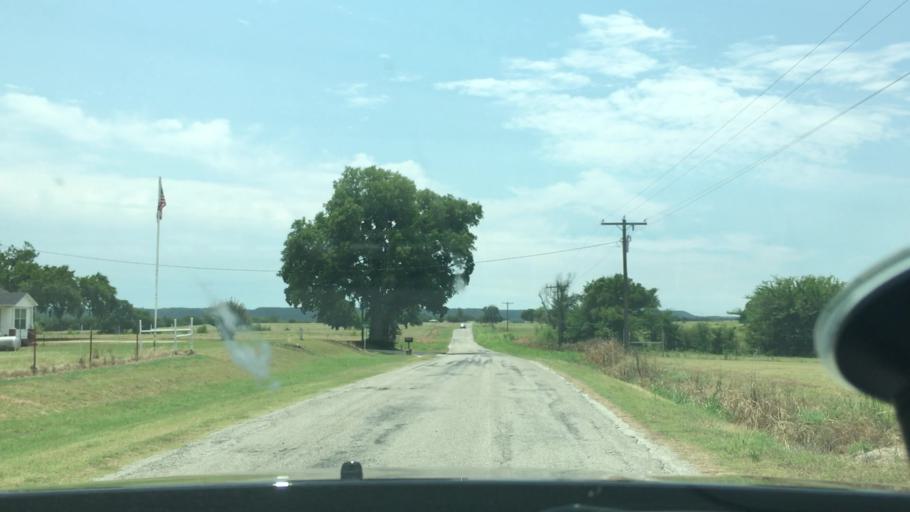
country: US
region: Texas
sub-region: Cooke County
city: Muenster
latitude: 33.8819
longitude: -97.3566
